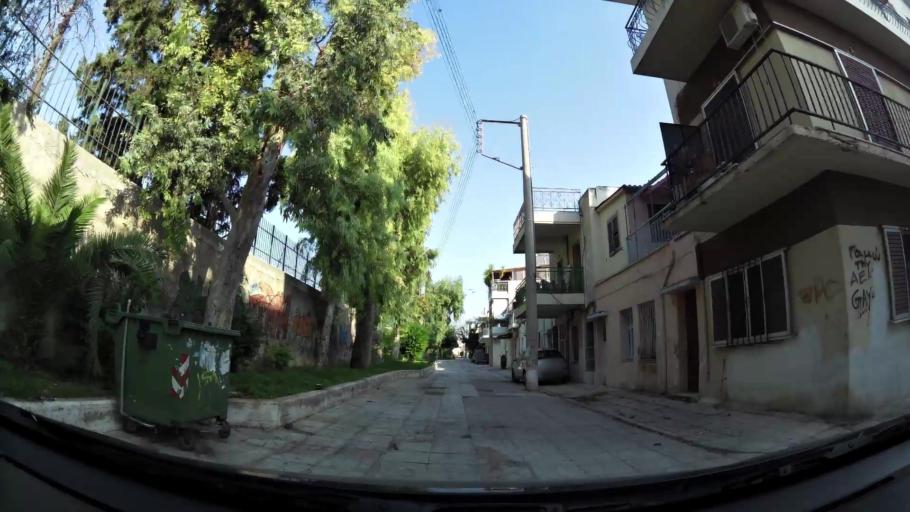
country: GR
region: Attica
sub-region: Nomos Piraios
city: Drapetsona
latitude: 37.9554
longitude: 23.6257
